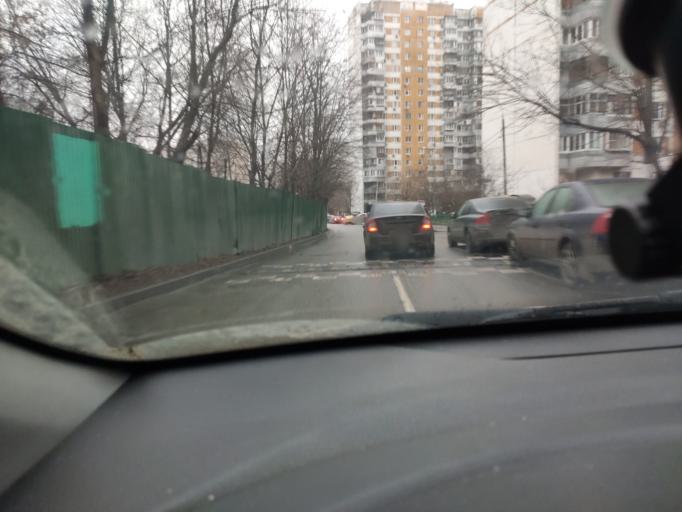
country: RU
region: Moscow
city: Chertanovo Yuzhnoye
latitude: 55.5938
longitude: 37.5936
